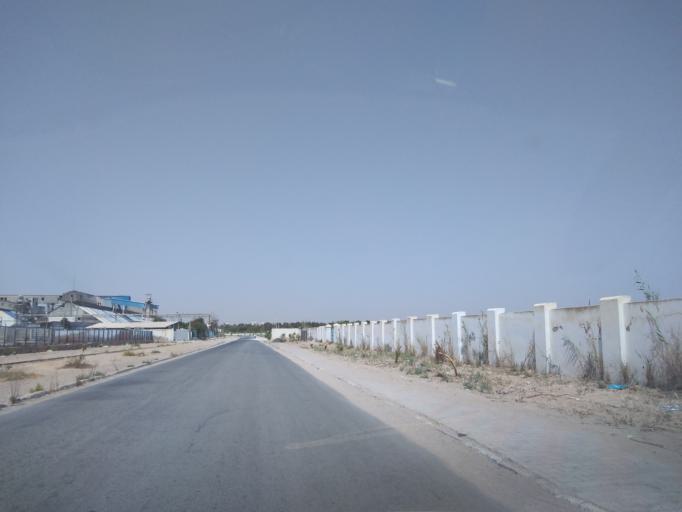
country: TN
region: Safaqis
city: Al Qarmadah
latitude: 34.7297
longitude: 10.7790
